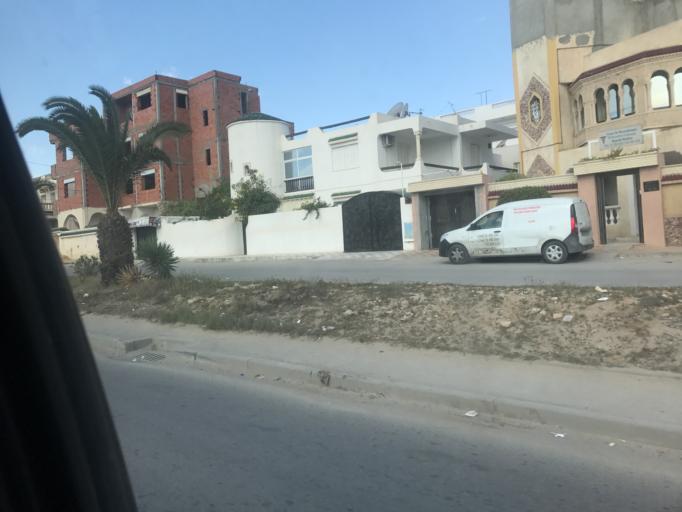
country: TN
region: Susah
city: Sousse
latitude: 35.8017
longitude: 10.6126
